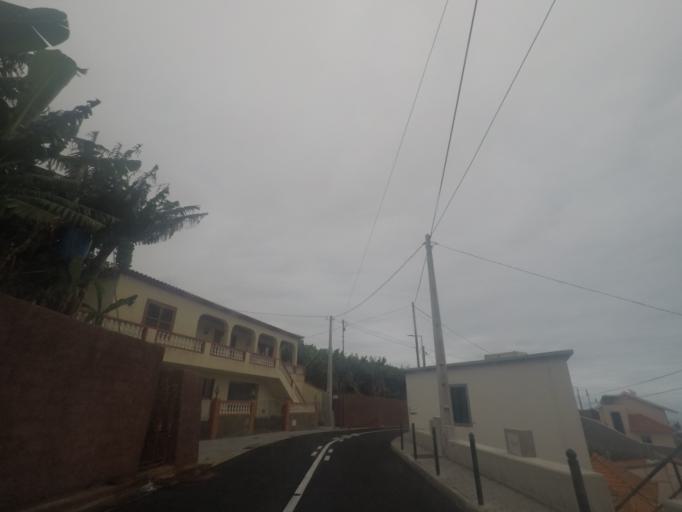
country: PT
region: Madeira
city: Camara de Lobos
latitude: 32.6636
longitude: -16.9713
